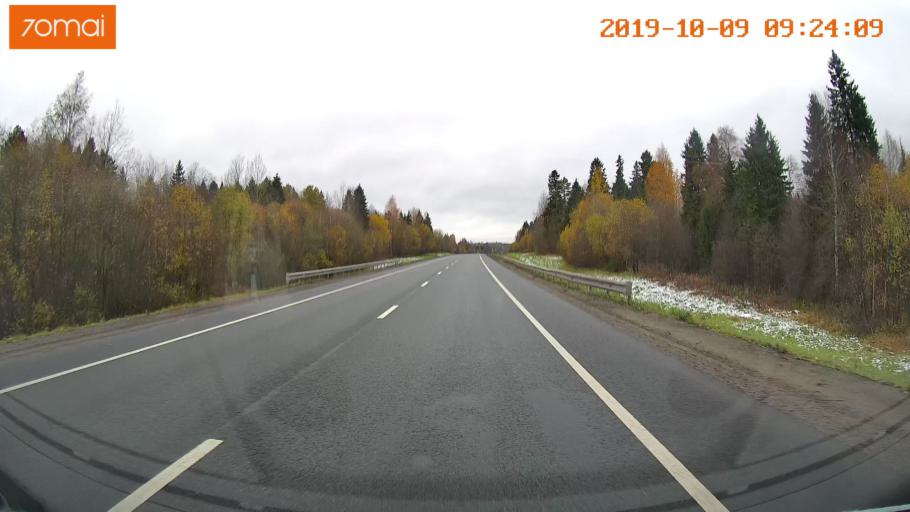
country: RU
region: Vologda
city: Vologda
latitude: 59.0759
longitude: 40.0206
